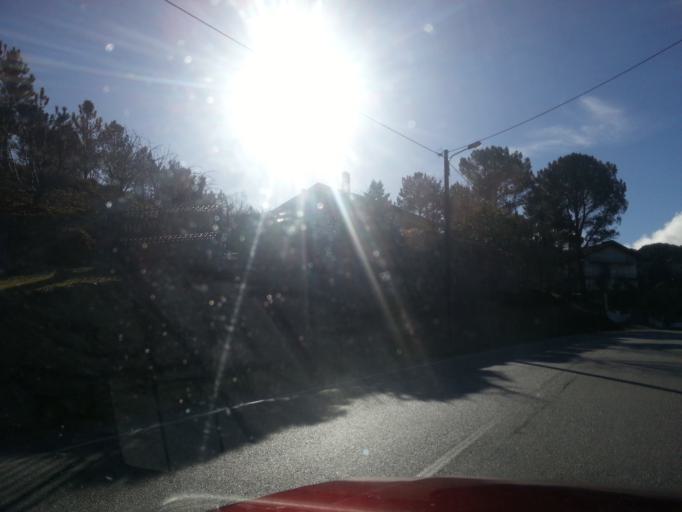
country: PT
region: Guarda
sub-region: Guarda
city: Guarda
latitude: 40.5414
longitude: -7.3159
